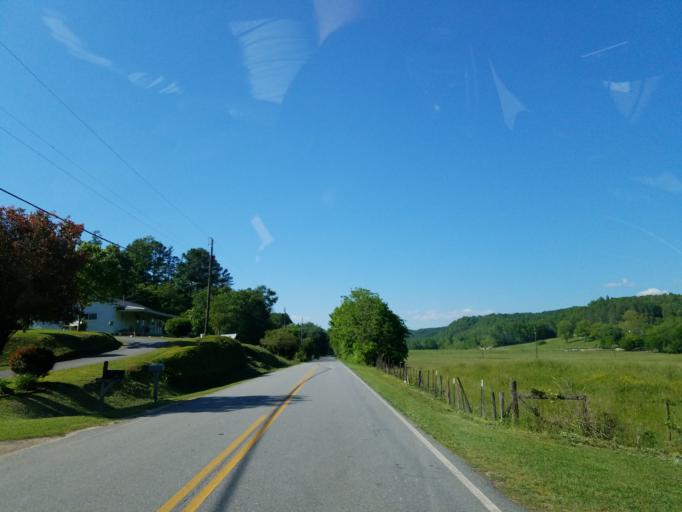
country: US
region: Georgia
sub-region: Pickens County
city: Jasper
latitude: 34.5629
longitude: -84.5116
